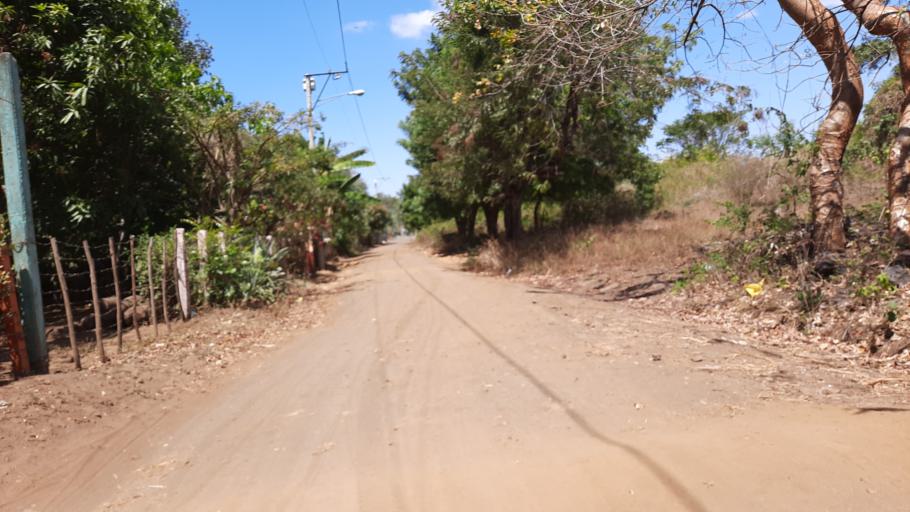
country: NI
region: Masaya
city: Ticuantepe
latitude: 12.0293
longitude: -86.1670
